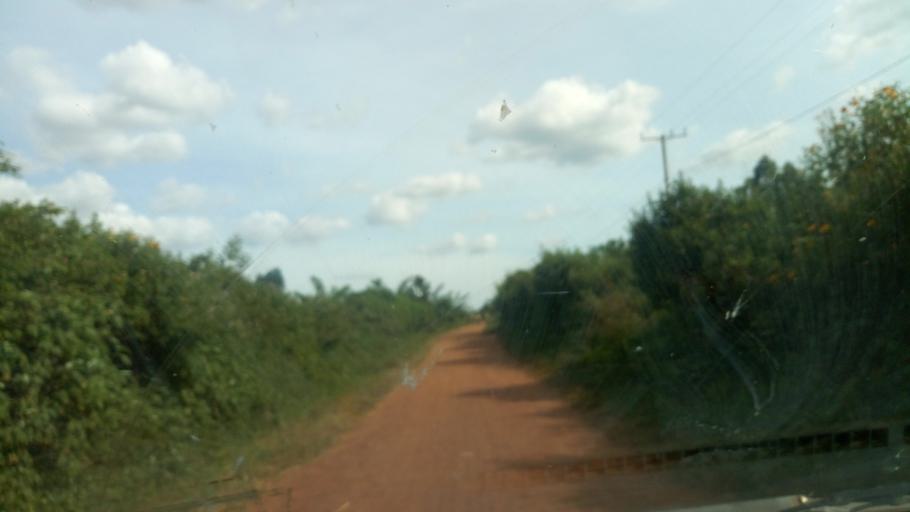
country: UG
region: Western Region
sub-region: Kiryandongo District
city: Kiryandongo
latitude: 1.8125
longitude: 31.9395
